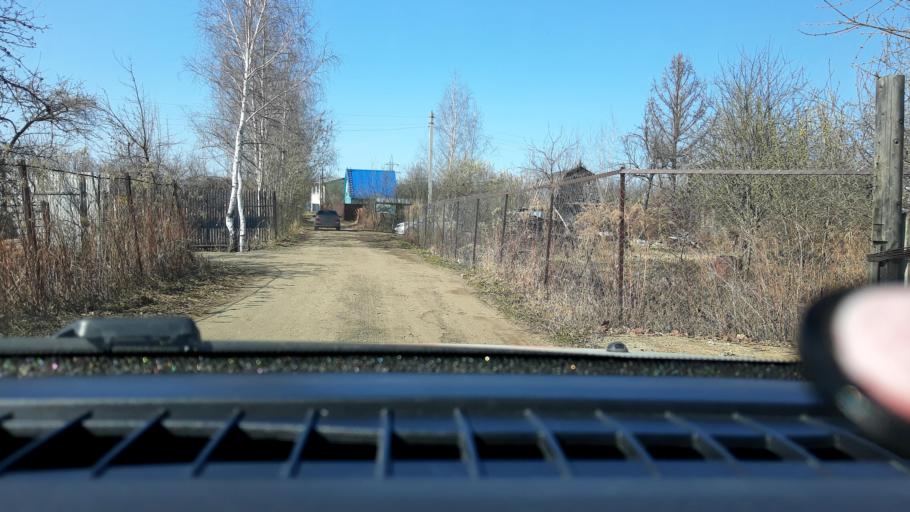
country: RU
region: Nizjnij Novgorod
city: Gorbatovka
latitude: 56.2636
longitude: 43.8234
